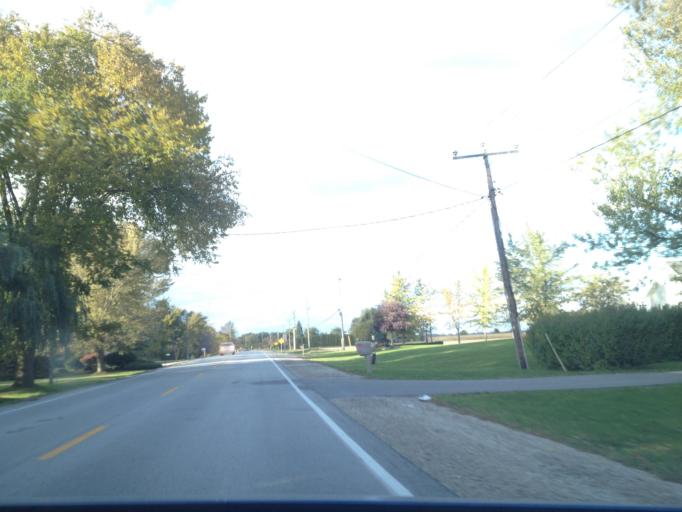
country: US
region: Michigan
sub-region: Wayne County
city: Grosse Pointe Farms
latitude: 42.2469
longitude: -82.7128
